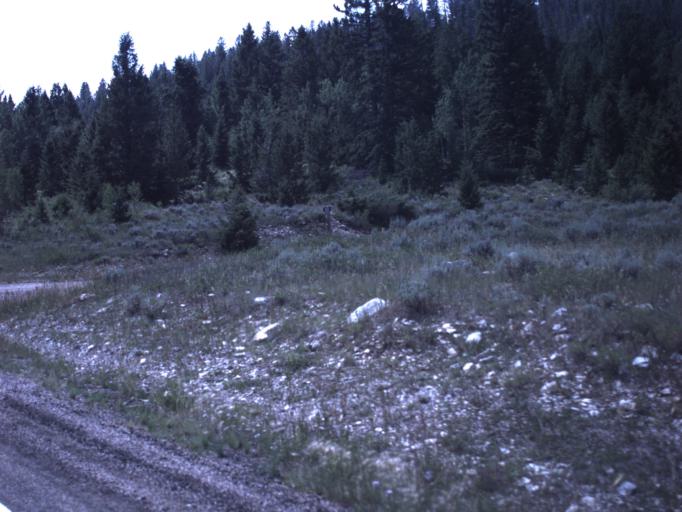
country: US
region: Utah
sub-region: Uintah County
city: Maeser
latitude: 40.7045
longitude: -109.4935
